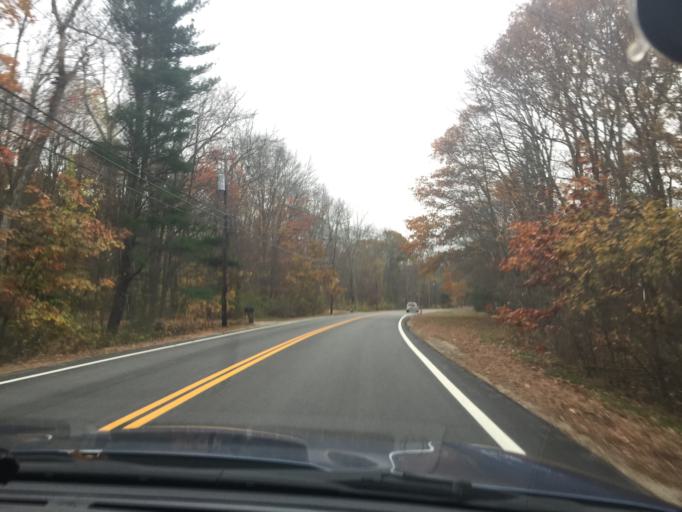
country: US
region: Rhode Island
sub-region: Providence County
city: Foster
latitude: 41.8583
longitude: -71.7133
